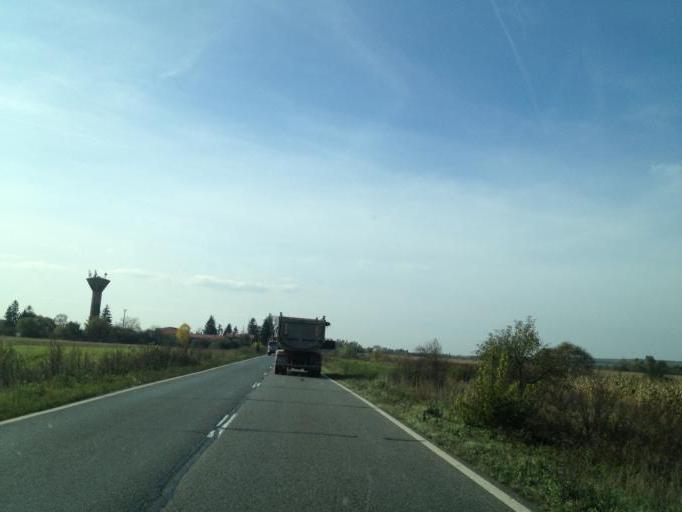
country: RO
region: Timis
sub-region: Comuna Faget
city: Faget
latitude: 45.8584
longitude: 22.1982
